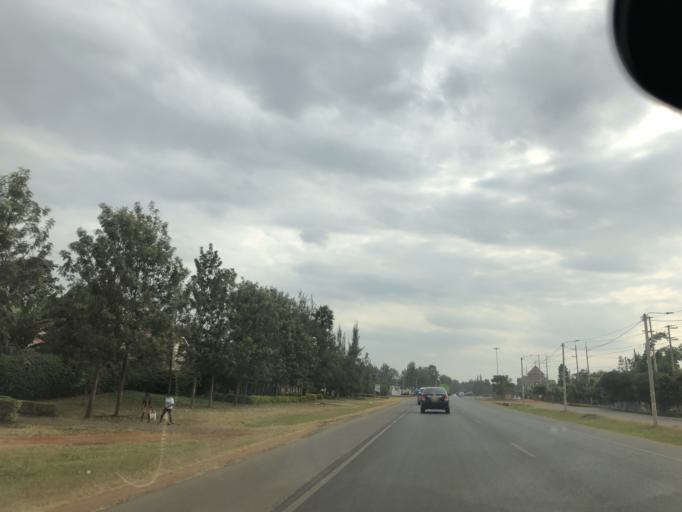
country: KE
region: Kiambu
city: Kiambu
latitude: -1.2137
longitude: 36.8699
